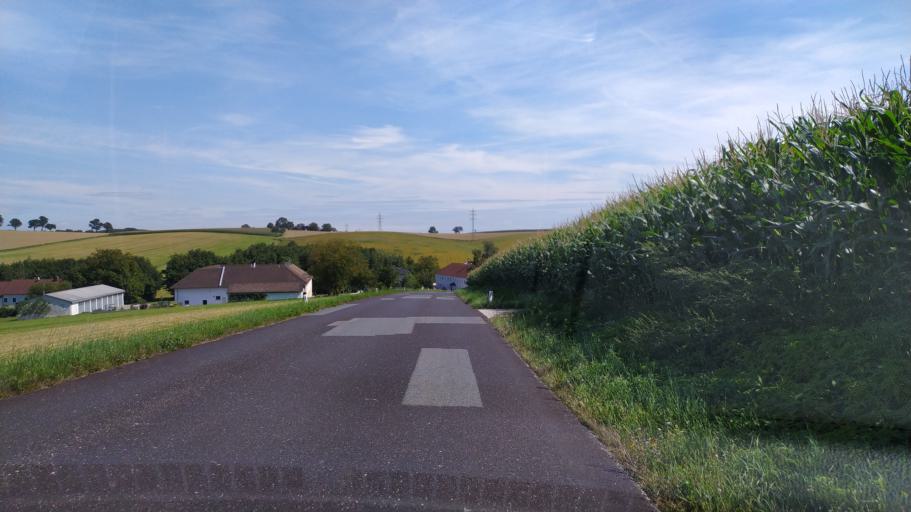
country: AT
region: Lower Austria
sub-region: Politischer Bezirk Amstetten
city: Wolfsbach
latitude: 48.1105
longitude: 14.6968
